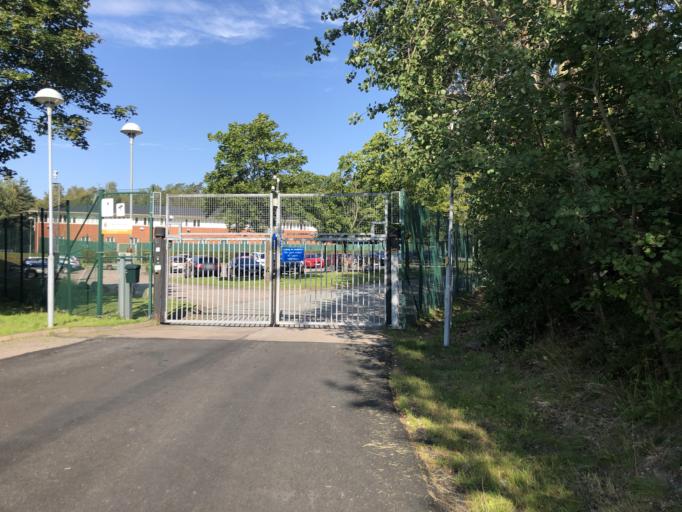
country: SE
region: Vaestra Goetaland
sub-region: Goteborg
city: Goeteborg
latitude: 57.7481
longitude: 11.9646
